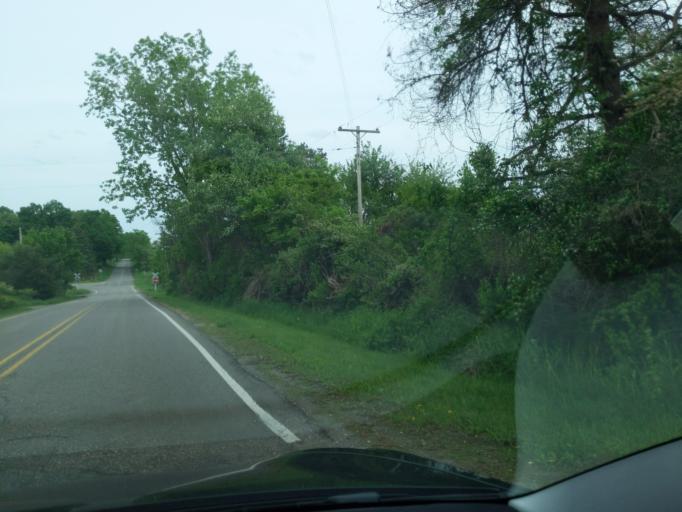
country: US
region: Michigan
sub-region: Ingham County
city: Mason
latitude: 42.5332
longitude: -84.4253
